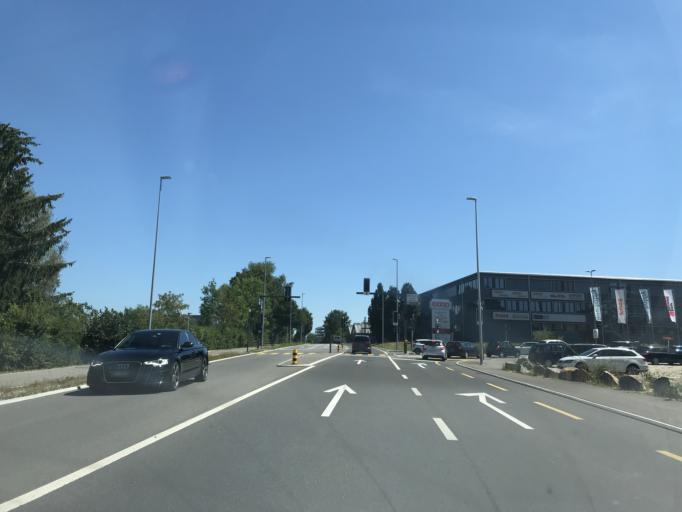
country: CH
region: Aargau
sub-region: Bezirk Rheinfelden
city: Kaiseraugst
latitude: 47.5379
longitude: 7.7285
